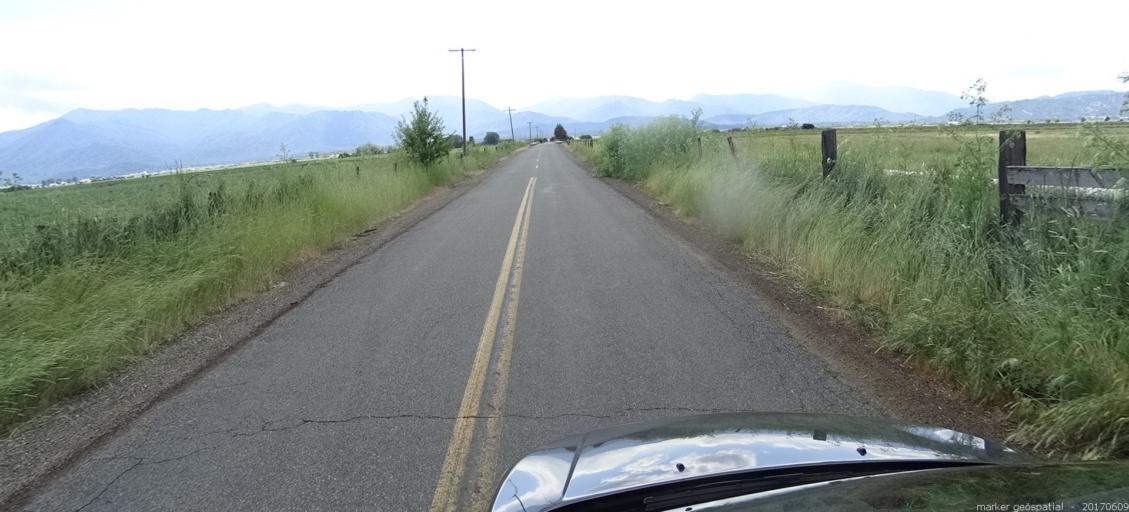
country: US
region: California
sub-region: Siskiyou County
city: Yreka
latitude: 41.5194
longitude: -122.8520
